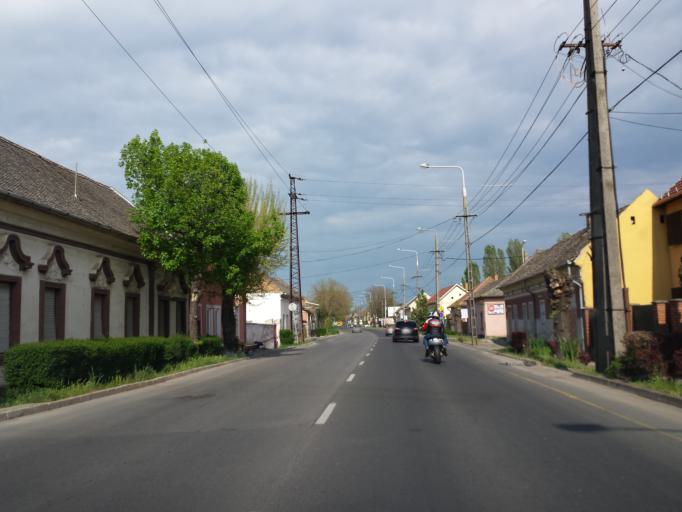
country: HU
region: Csongrad
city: Mako
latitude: 46.2104
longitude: 20.4639
